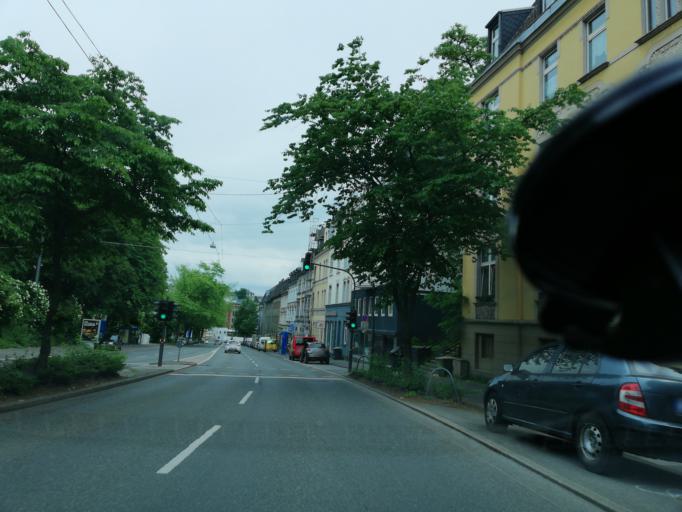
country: DE
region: North Rhine-Westphalia
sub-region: Regierungsbezirk Dusseldorf
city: Wuppertal
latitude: 51.2763
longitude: 7.1871
